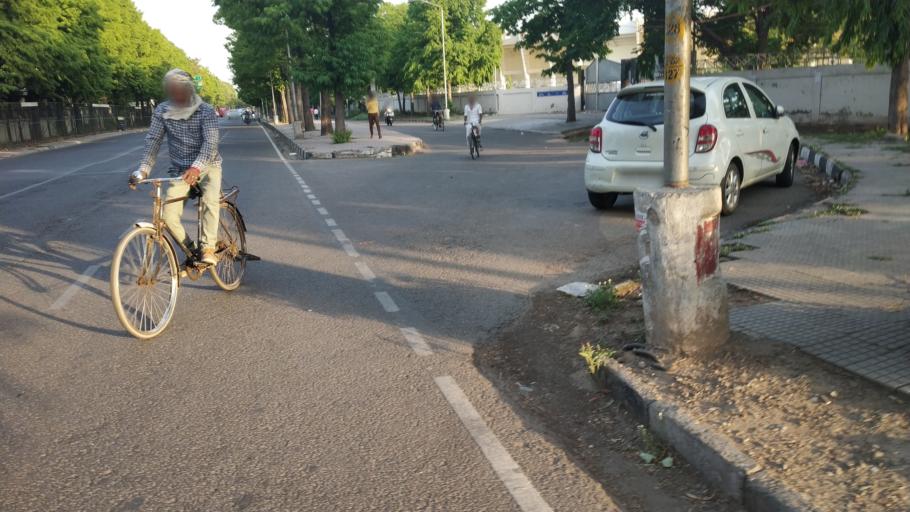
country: IN
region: Punjab
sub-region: Ajitgarh
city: Mohali
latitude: 30.6909
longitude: 76.7358
